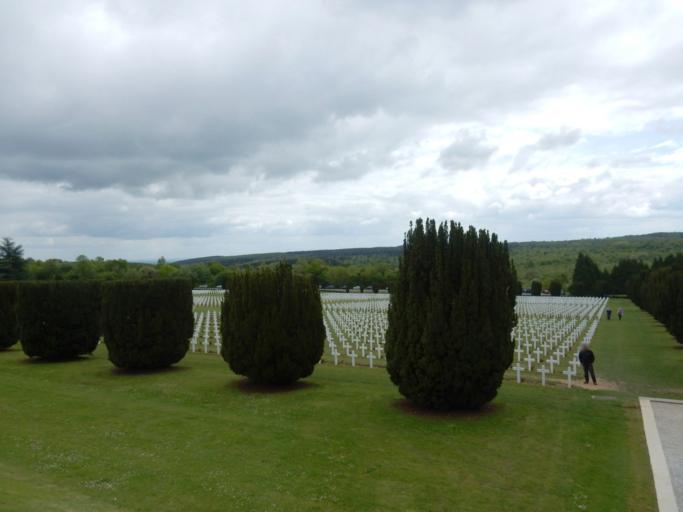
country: FR
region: Lorraine
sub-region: Departement de la Meuse
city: Verdun
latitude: 49.2080
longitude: 5.4242
